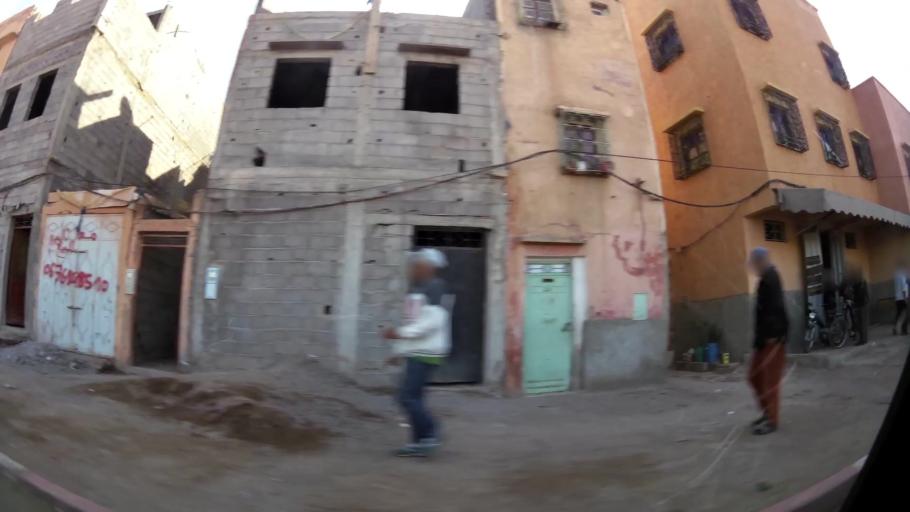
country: MA
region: Marrakech-Tensift-Al Haouz
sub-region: Marrakech
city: Marrakesh
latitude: 31.6184
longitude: -7.9652
